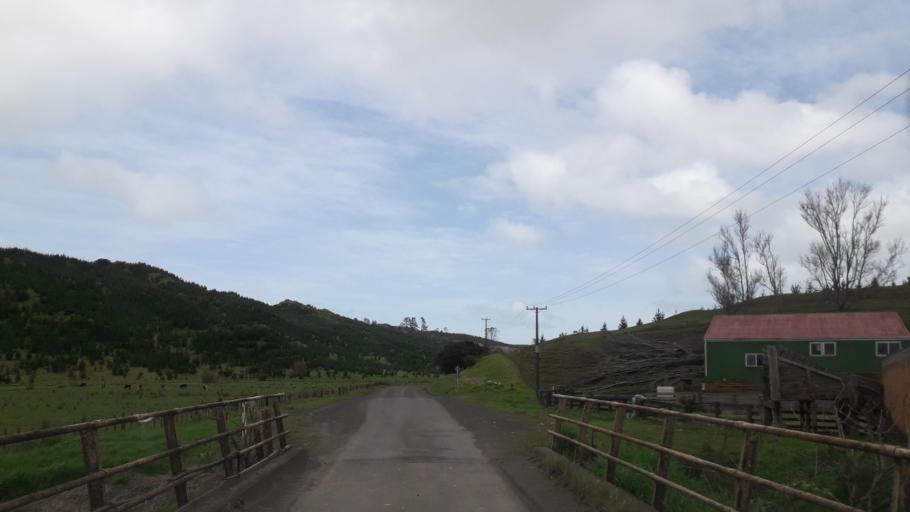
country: NZ
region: Northland
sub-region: Far North District
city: Ahipara
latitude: -35.4249
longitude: 173.3574
